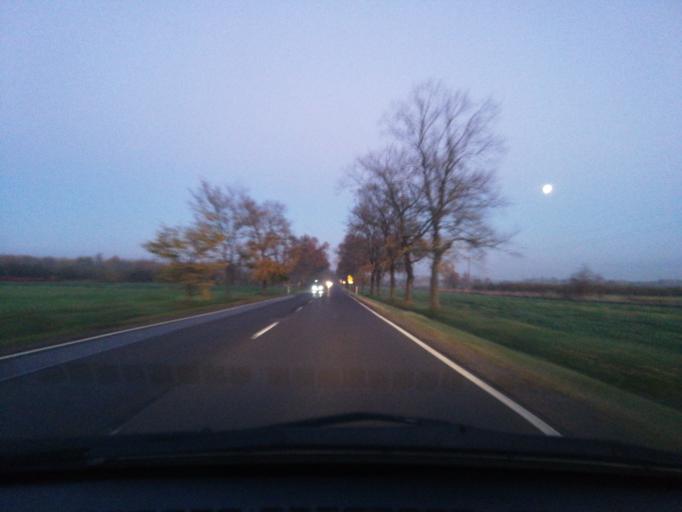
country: PL
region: Lodz Voivodeship
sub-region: Powiat brzezinski
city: Rogow
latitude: 51.8064
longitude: 19.8829
